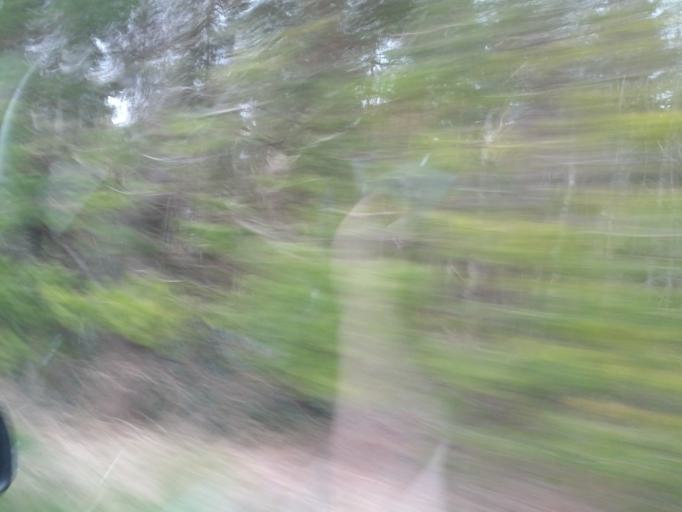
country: IE
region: Connaught
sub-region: County Galway
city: Athenry
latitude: 53.3840
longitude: -8.6401
